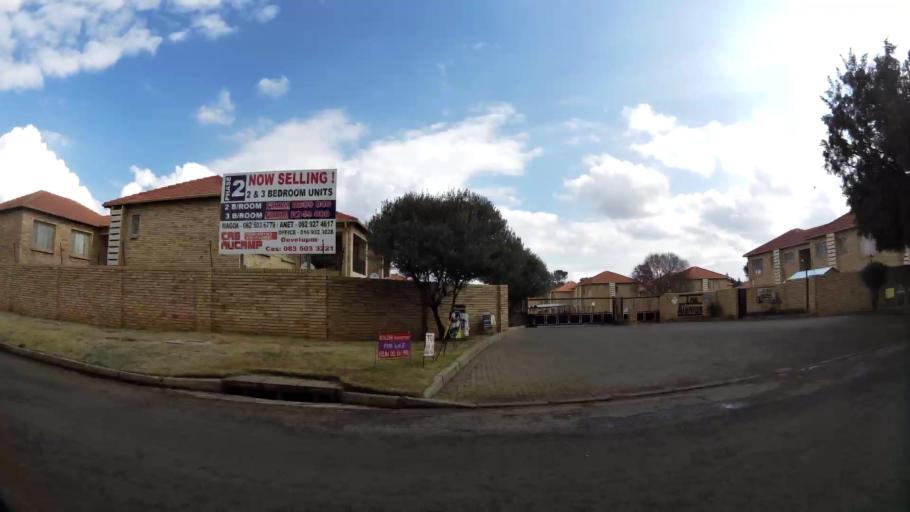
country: ZA
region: Gauteng
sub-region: Sedibeng District Municipality
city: Vanderbijlpark
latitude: -26.7454
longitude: 27.8284
